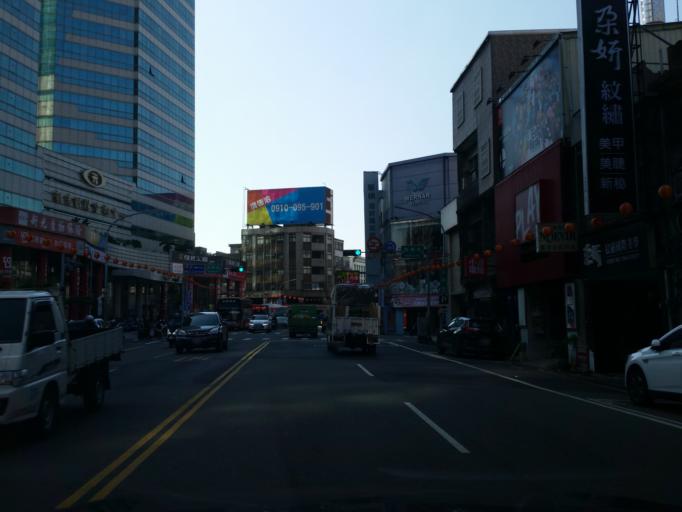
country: TW
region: Taiwan
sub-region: Taoyuan
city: Taoyuan
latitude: 24.9893
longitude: 121.3094
